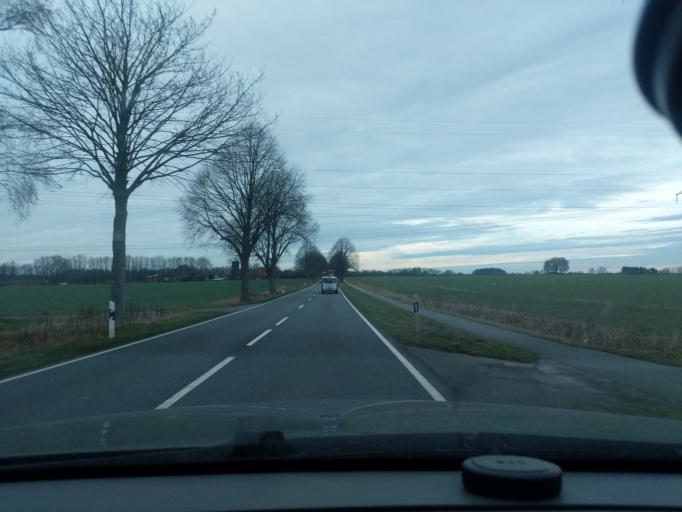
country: DE
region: Lower Saxony
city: Sauensiek
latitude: 53.3989
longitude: 9.6102
